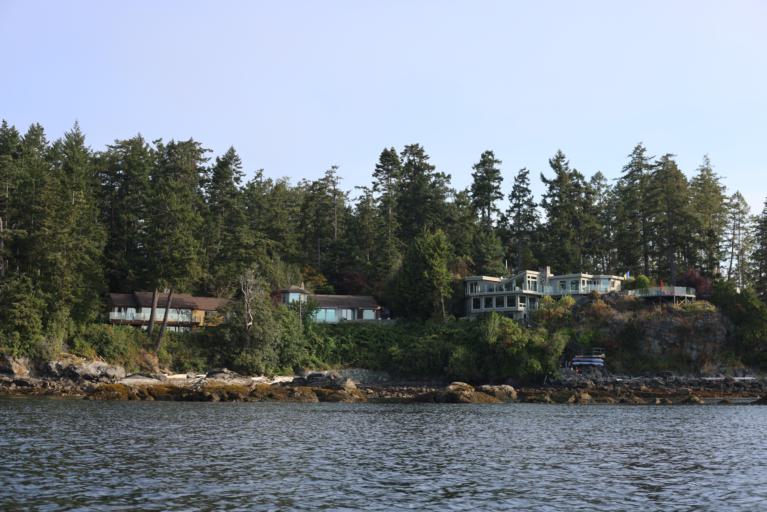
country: CA
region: British Columbia
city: North Saanich
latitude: 48.6737
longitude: -123.4009
